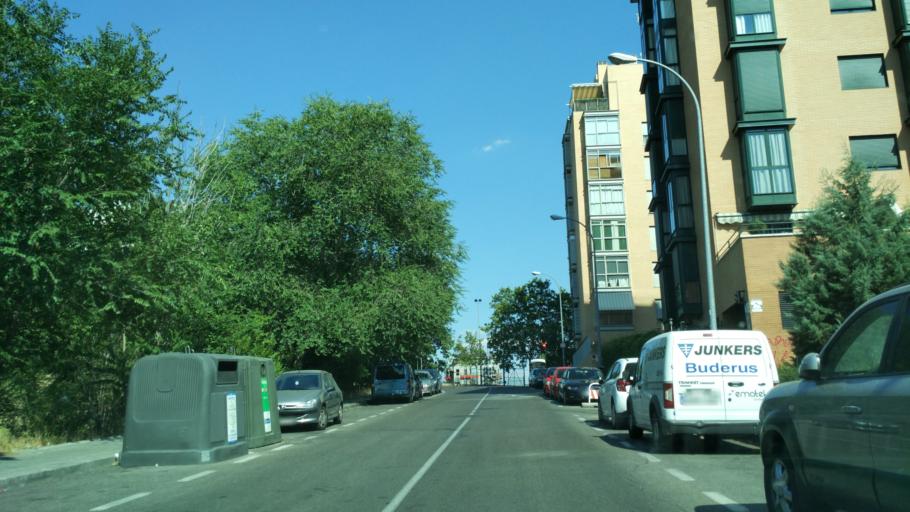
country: ES
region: Madrid
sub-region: Provincia de Madrid
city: Tetuan de las Victorias
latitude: 40.4723
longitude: -3.7212
